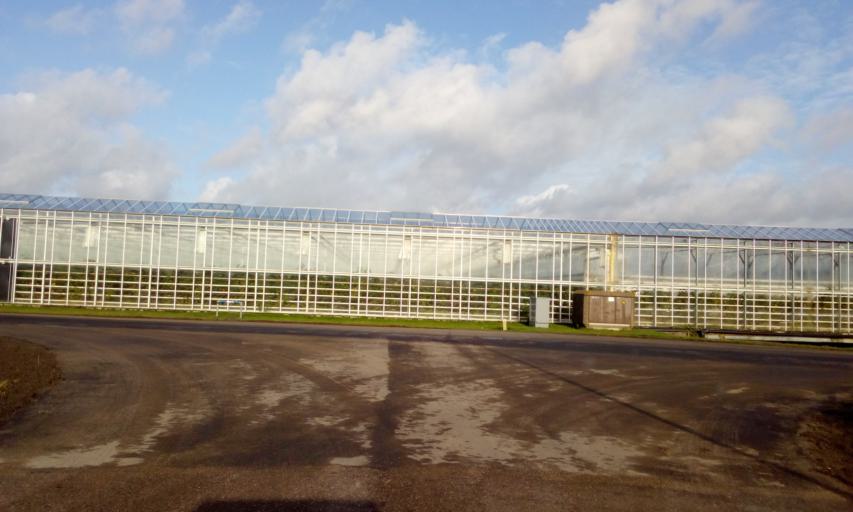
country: NL
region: South Holland
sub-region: Gemeente Lansingerland
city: Berkel en Rodenrijs
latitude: 52.0180
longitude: 4.4908
